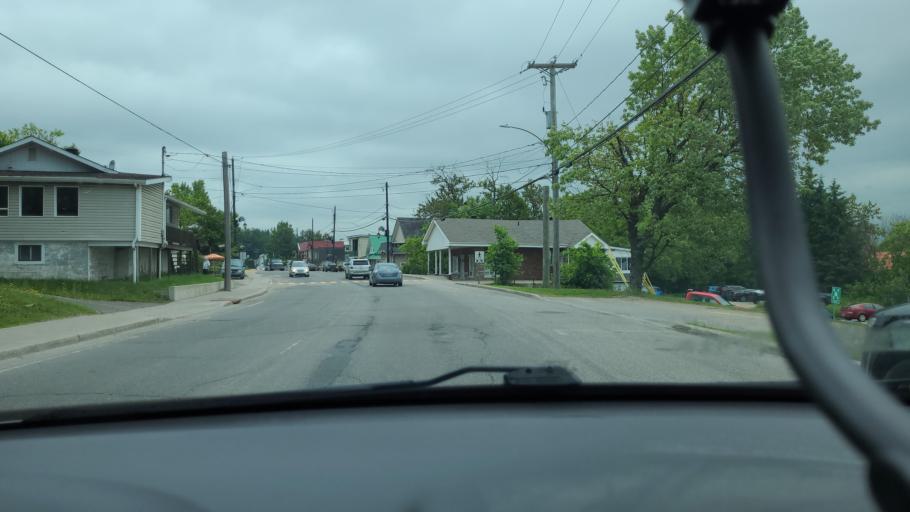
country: CA
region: Quebec
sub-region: Laurentides
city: Riviere-Rouge
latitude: 46.4065
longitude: -74.8670
